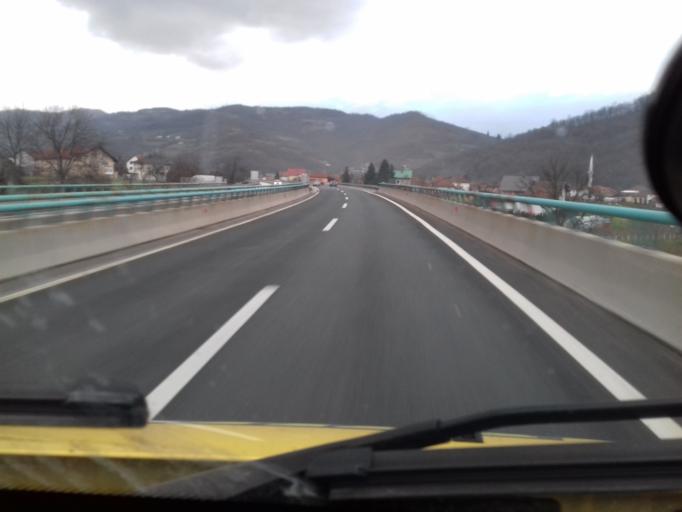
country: BA
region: Federation of Bosnia and Herzegovina
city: Ilijas
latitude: 43.9496
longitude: 18.2547
